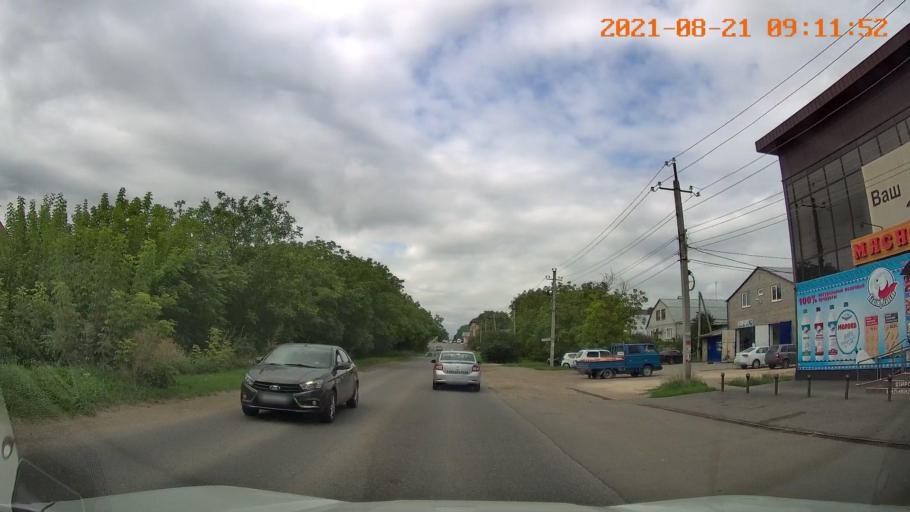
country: RU
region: Stavropol'skiy
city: Svobody
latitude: 44.0159
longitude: 43.0674
